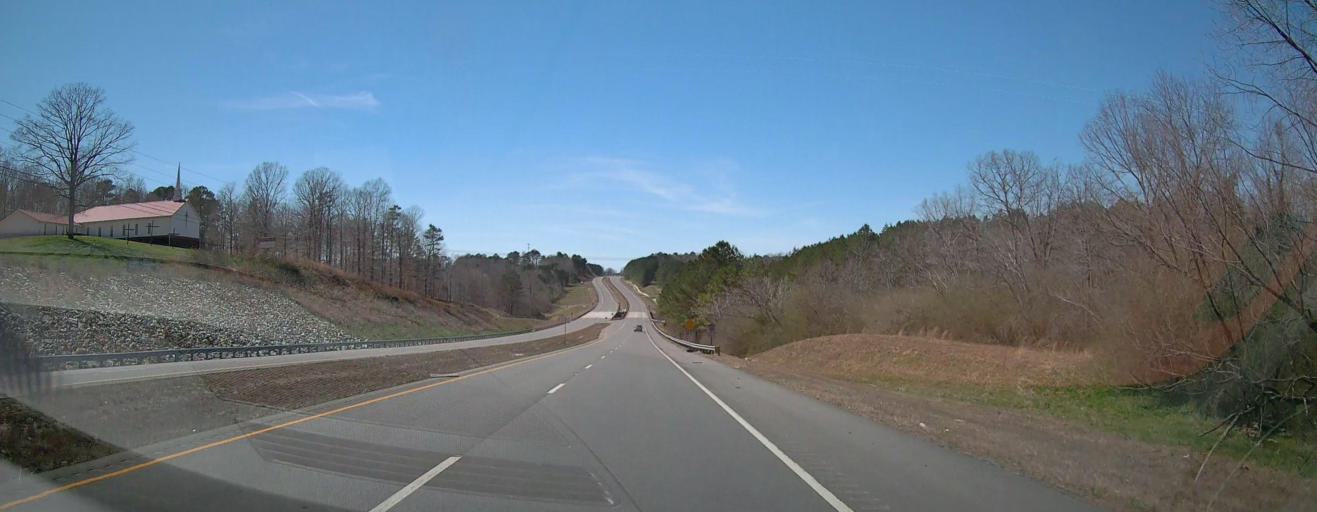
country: US
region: Alabama
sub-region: Cullman County
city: Cullman
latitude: 34.1823
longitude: -86.7691
